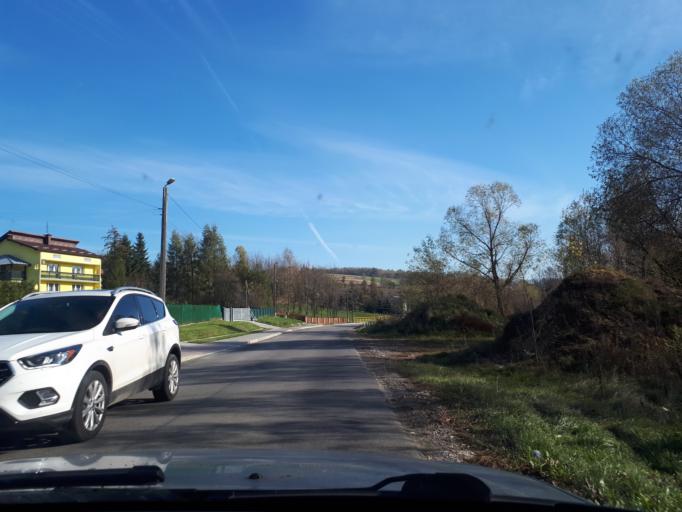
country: PL
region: Subcarpathian Voivodeship
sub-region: Powiat debicki
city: Debica
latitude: 50.0039
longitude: 21.4046
